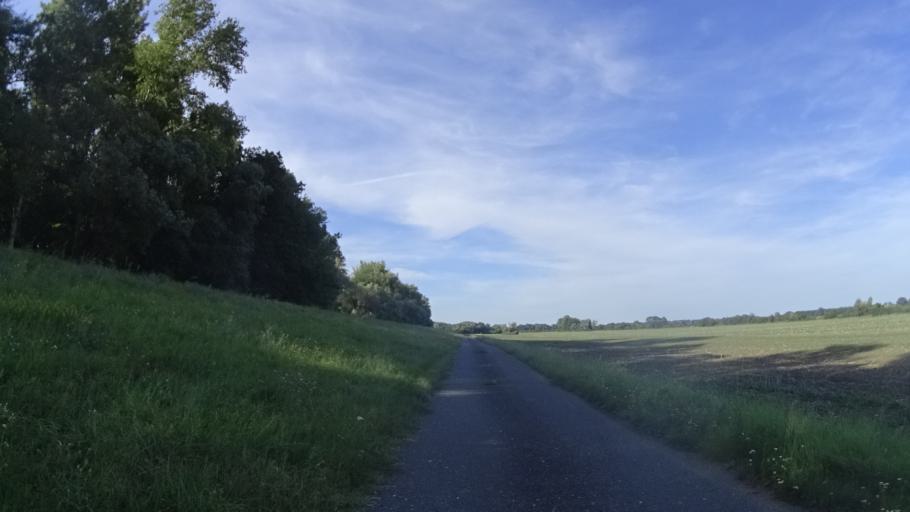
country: AT
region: Lower Austria
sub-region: Politischer Bezirk Ganserndorf
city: Drosing
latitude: 48.5260
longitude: 16.9552
